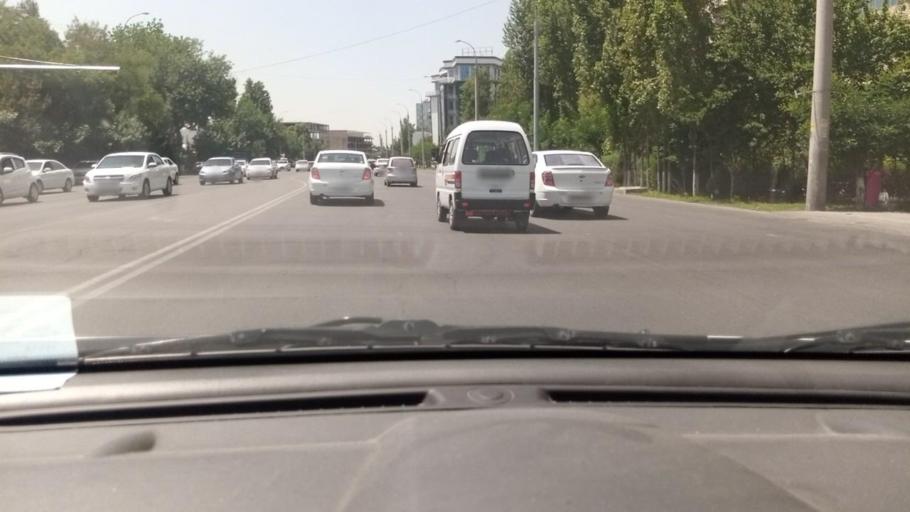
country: UZ
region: Toshkent Shahri
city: Tashkent
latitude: 41.2683
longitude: 69.2521
